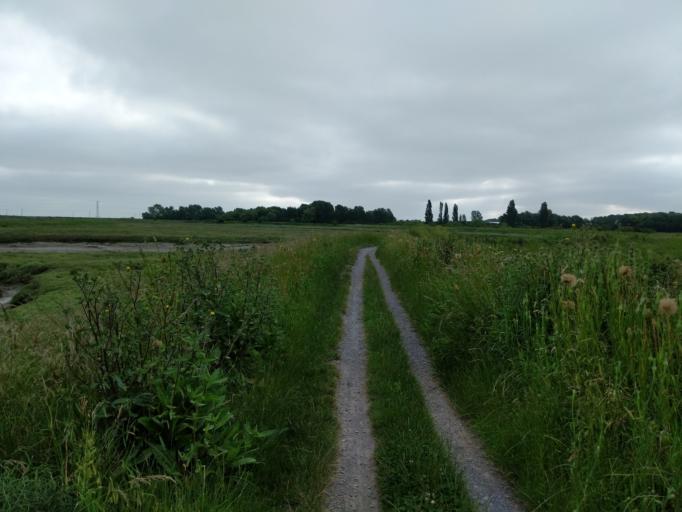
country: GB
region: England
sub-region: Kent
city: Faversham
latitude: 51.3259
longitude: 0.9125
